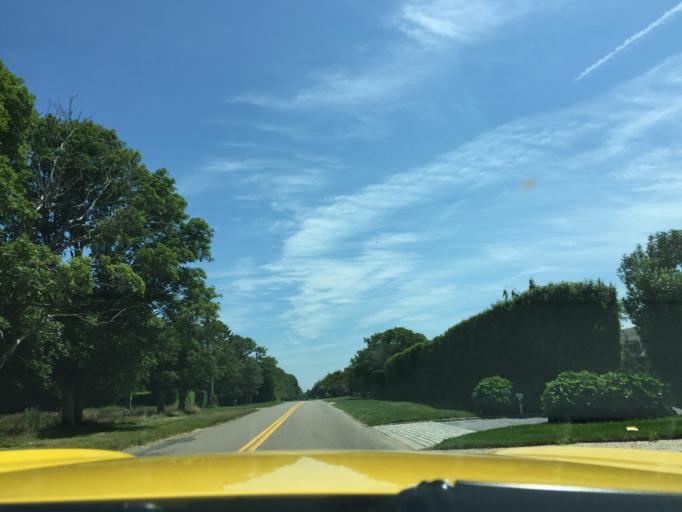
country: US
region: New York
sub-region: Suffolk County
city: Bridgehampton
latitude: 40.9332
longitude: -72.2697
